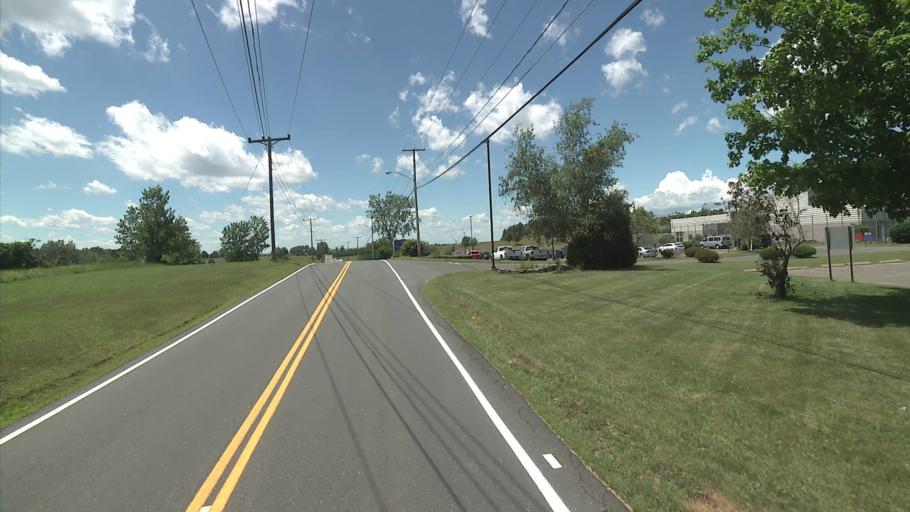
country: US
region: Massachusetts
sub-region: Hampden County
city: East Longmeadow
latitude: 42.0165
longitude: -72.5057
